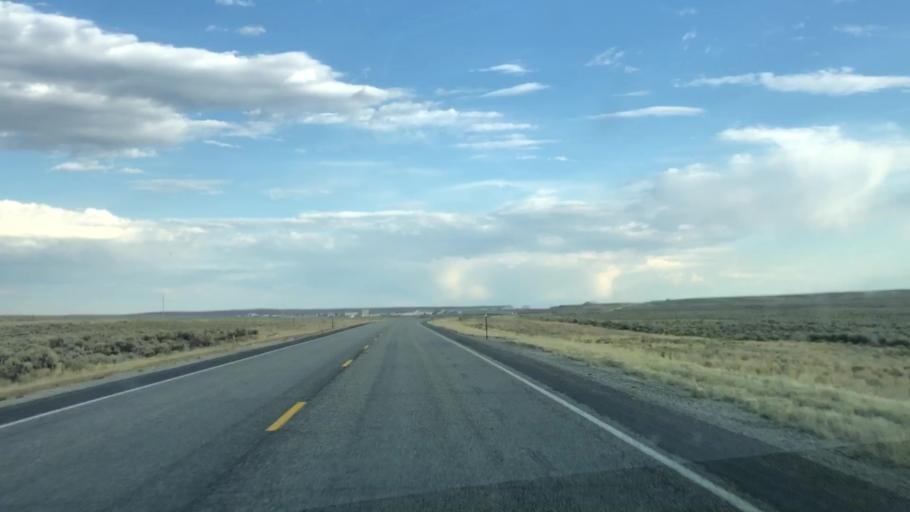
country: US
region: Wyoming
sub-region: Sublette County
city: Pinedale
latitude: 42.6213
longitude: -109.6520
